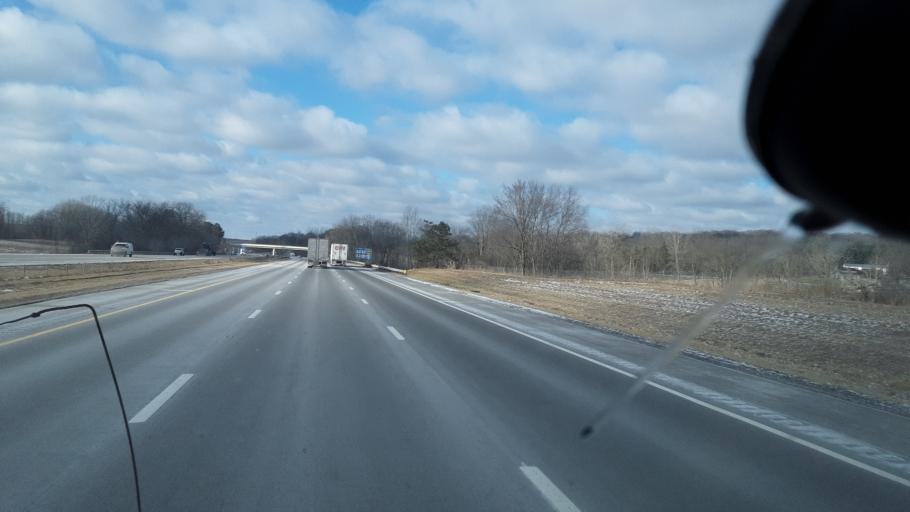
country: US
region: Ohio
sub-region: Ashland County
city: Ashland
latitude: 40.8686
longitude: -82.2343
